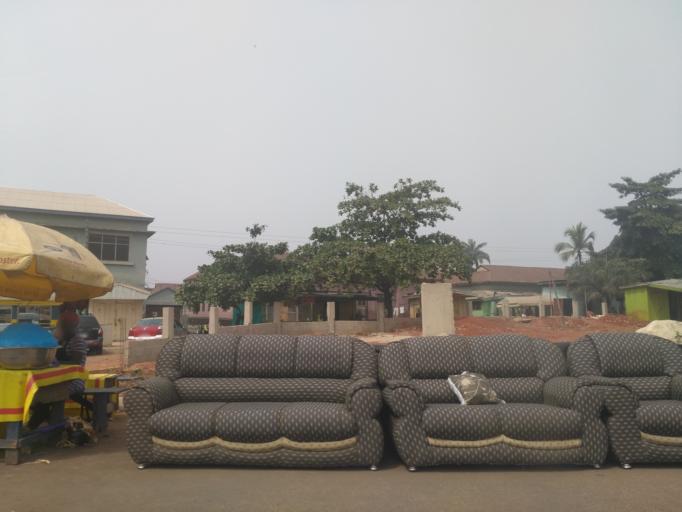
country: GH
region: Ashanti
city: Kumasi
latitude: 6.7021
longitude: -1.6164
